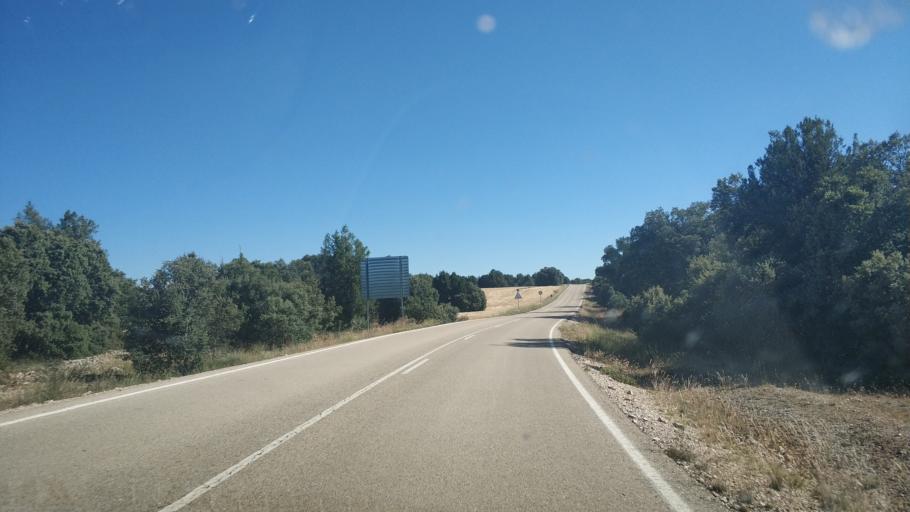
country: ES
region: Castille and Leon
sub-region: Provincia de Soria
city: Liceras
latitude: 41.4574
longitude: -3.2112
